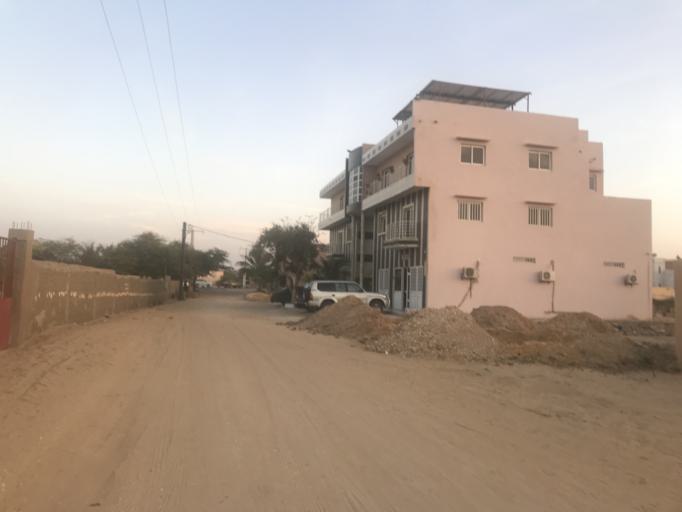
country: SN
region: Saint-Louis
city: Saint-Louis
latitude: 16.0493
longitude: -16.4336
